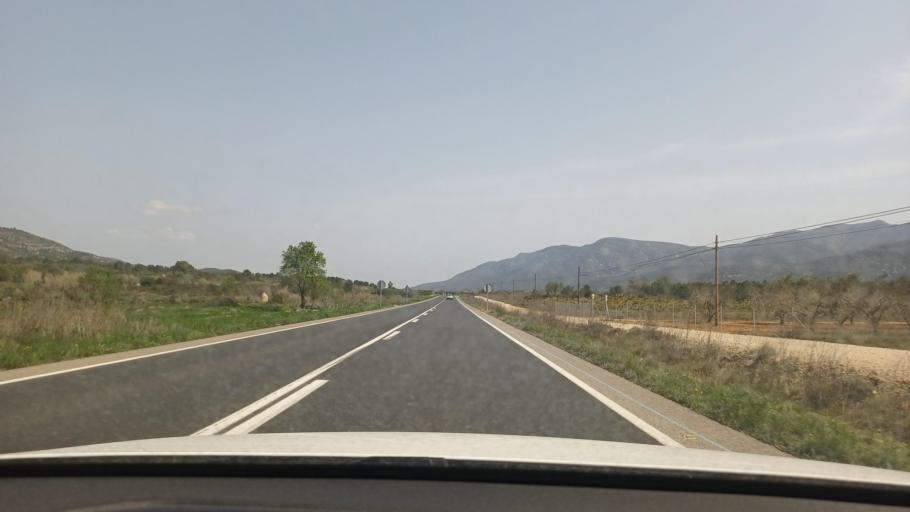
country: ES
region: Catalonia
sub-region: Provincia de Tarragona
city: Ulldecona
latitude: 40.6215
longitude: 0.4725
